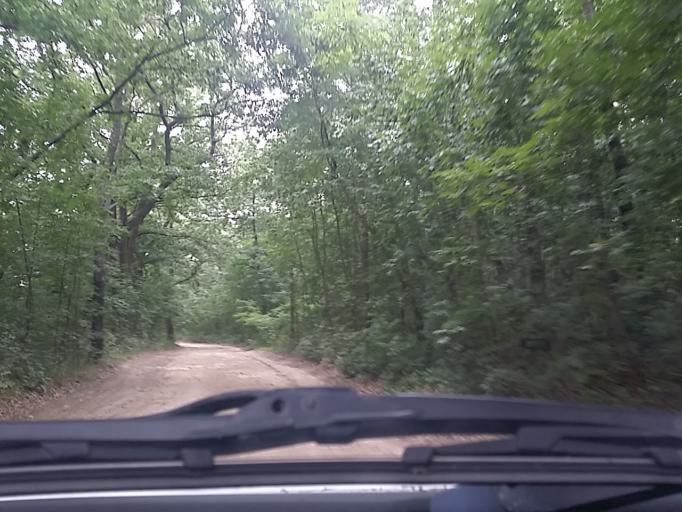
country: HU
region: Pest
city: Csobanka
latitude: 47.6475
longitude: 18.9444
